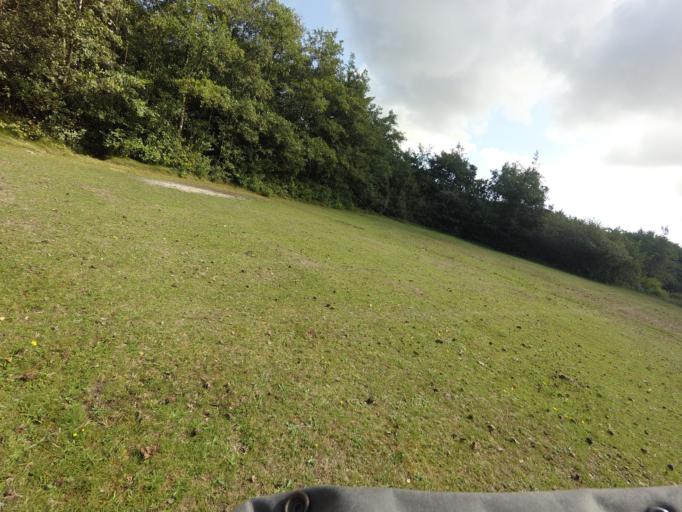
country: NL
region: Friesland
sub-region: Gemeente Terschelling
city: West-Terschelling
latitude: 53.3771
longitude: 5.2105
